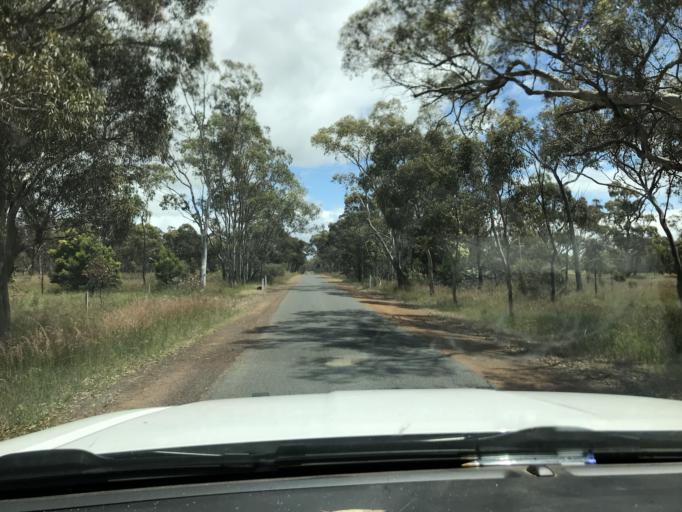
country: AU
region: Victoria
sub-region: Horsham
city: Horsham
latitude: -37.1215
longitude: 141.6971
